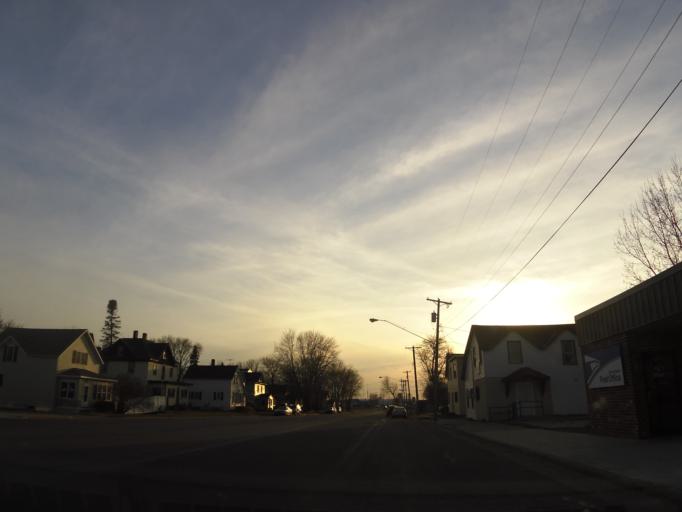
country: US
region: Minnesota
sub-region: Sibley County
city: Arlington
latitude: 44.6778
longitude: -94.0057
